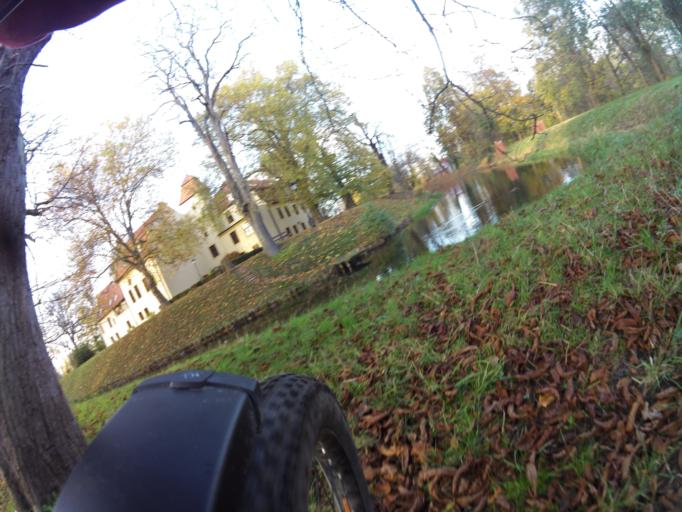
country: PL
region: Pomeranian Voivodeship
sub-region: Powiat pucki
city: Krokowa
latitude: 54.7764
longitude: 18.1646
